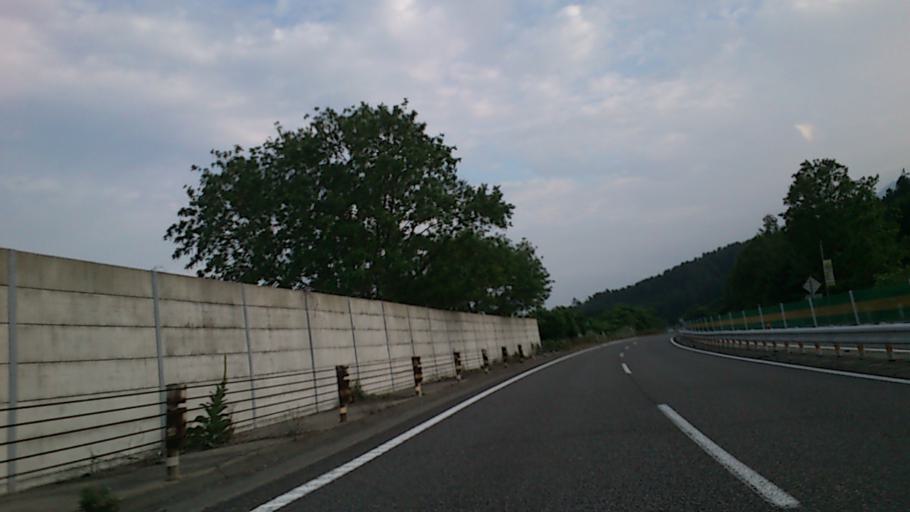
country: JP
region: Nagano
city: Ina
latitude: 35.7842
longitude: 137.9349
